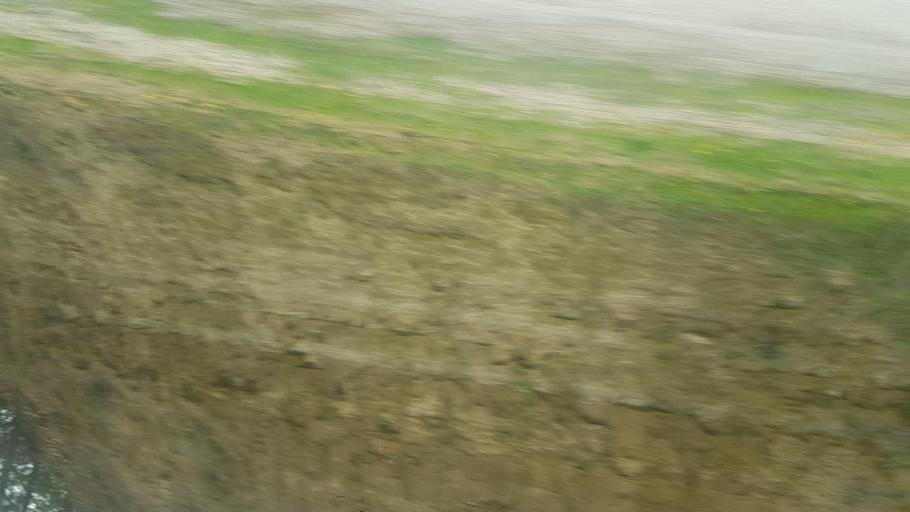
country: TR
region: Mersin
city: Yenice
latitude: 37.0854
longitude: 35.1721
